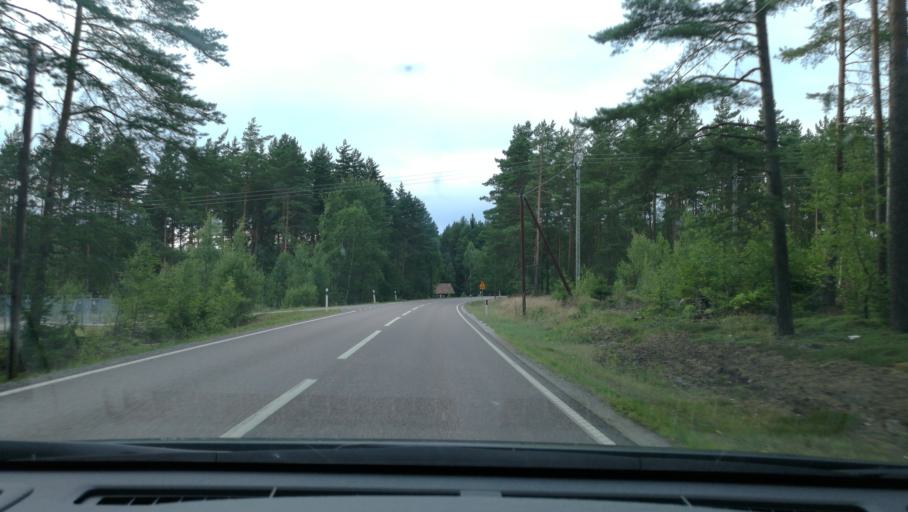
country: SE
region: Vaestmanland
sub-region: Kungsors Kommun
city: Kungsoer
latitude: 59.2977
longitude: 16.1074
